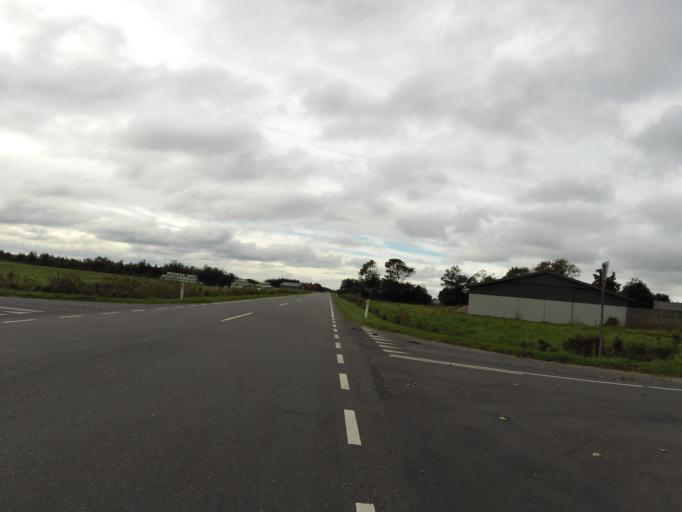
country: DK
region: South Denmark
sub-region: Tonder Kommune
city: Sherrebek
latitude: 55.2112
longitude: 8.8068
